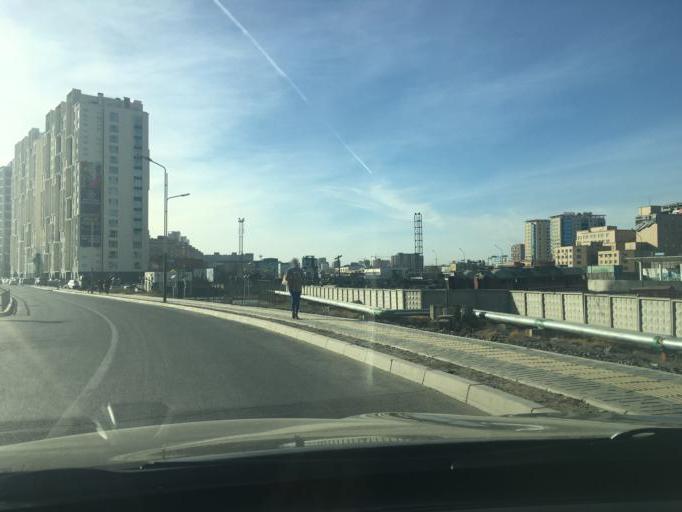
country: MN
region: Ulaanbaatar
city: Ulaanbaatar
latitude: 47.9071
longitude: 106.9123
